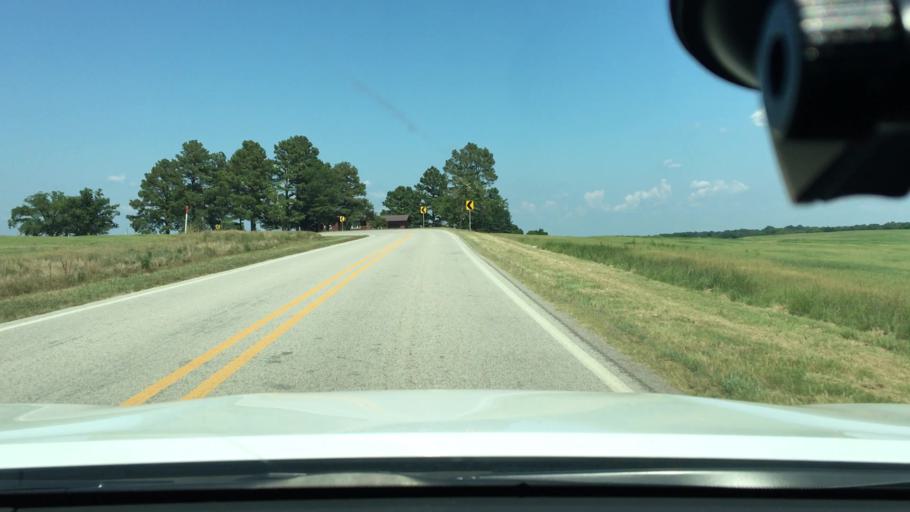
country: US
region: Arkansas
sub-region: Johnson County
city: Coal Hill
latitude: 35.3475
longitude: -93.5904
